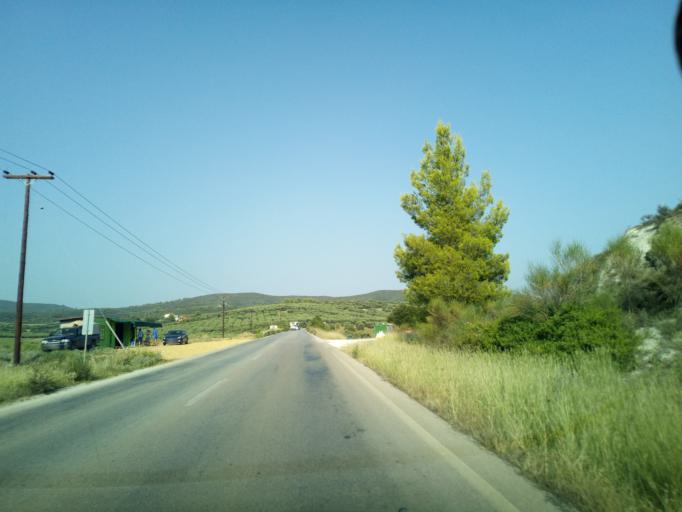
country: GR
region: Central Macedonia
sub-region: Nomos Chalkidikis
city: Ormylia
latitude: 40.2531
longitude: 23.5579
